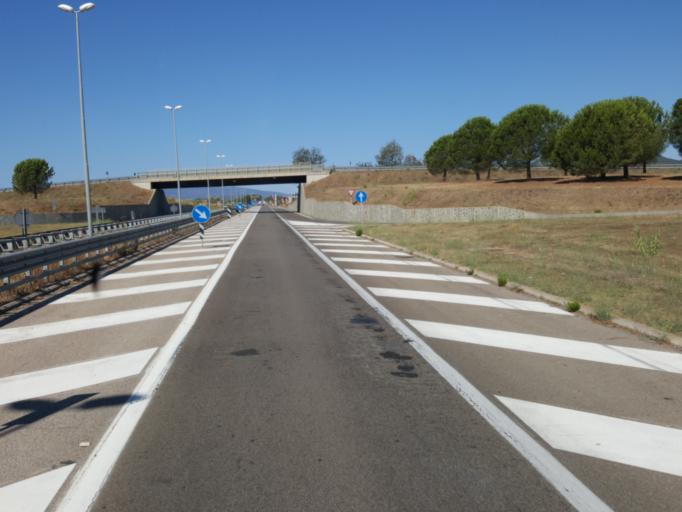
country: IT
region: Tuscany
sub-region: Provincia di Grosseto
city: Capalbio
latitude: 42.4147
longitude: 11.4118
